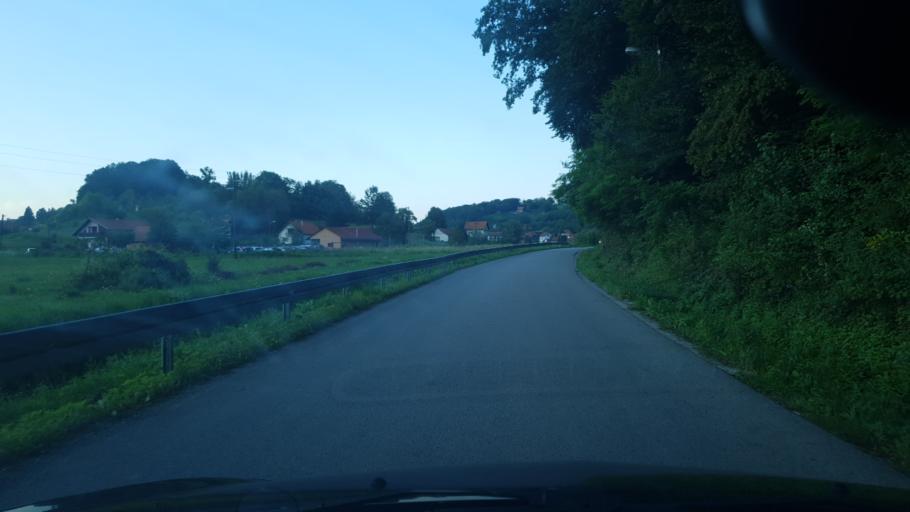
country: HR
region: Krapinsko-Zagorska
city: Zabok
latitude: 46.0260
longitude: 15.8940
